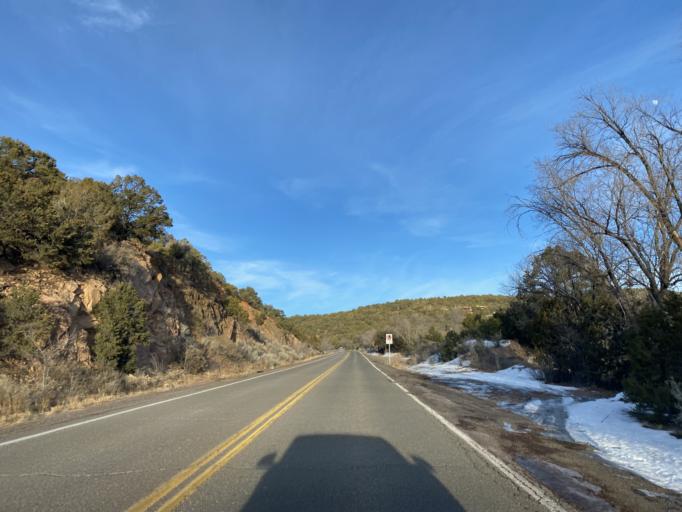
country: US
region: New Mexico
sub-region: Santa Fe County
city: Santa Fe
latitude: 35.7056
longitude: -105.9029
